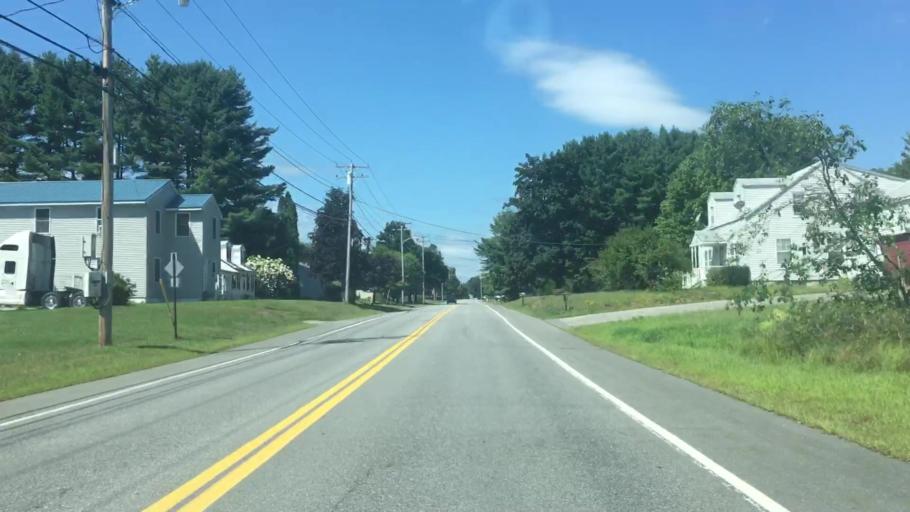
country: US
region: Maine
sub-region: Androscoggin County
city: Sabattus
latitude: 44.0931
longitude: -70.1512
